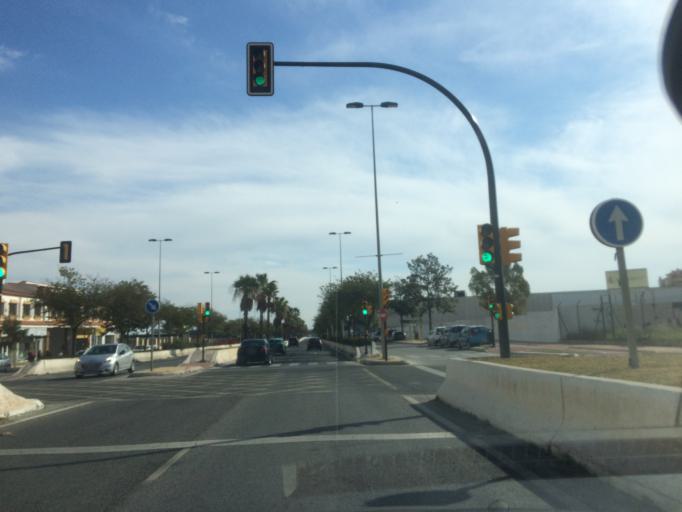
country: ES
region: Andalusia
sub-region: Provincia de Malaga
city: Torremolinos
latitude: 36.6606
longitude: -4.4998
